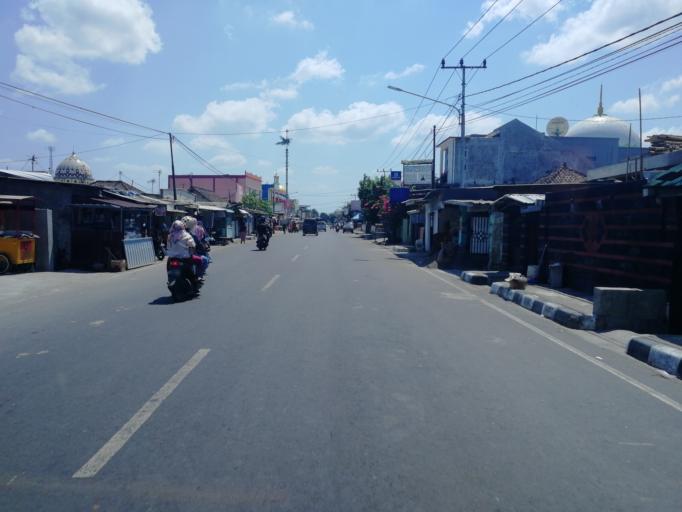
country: ID
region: West Nusa Tenggara
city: Kediri
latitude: -8.6881
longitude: 116.1207
